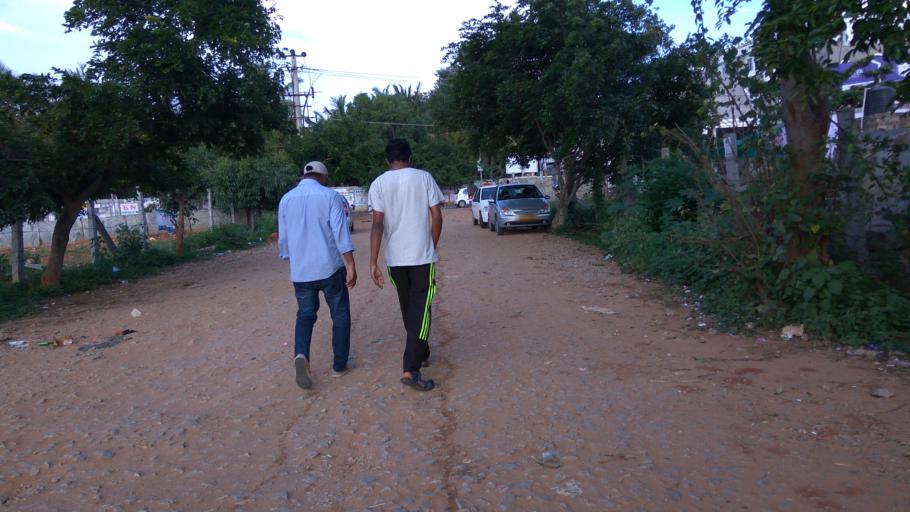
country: IN
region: Karnataka
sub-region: Bangalore Urban
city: Yelahanka
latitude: 13.1177
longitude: 77.6336
